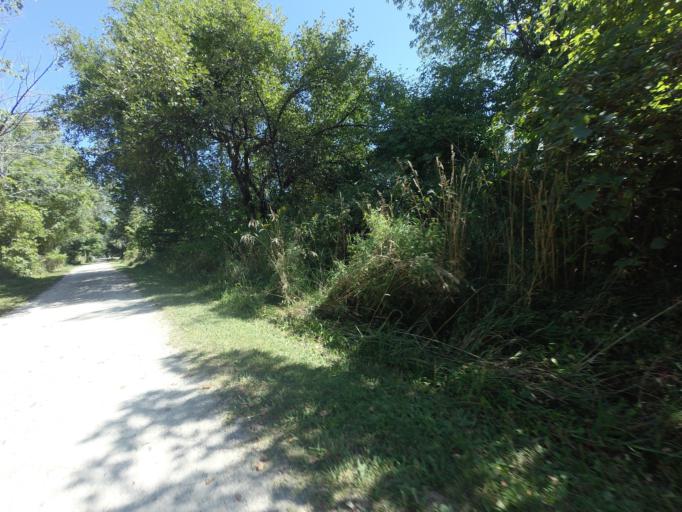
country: CA
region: Ontario
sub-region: Wellington County
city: Guelph
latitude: 43.7256
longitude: -80.3712
